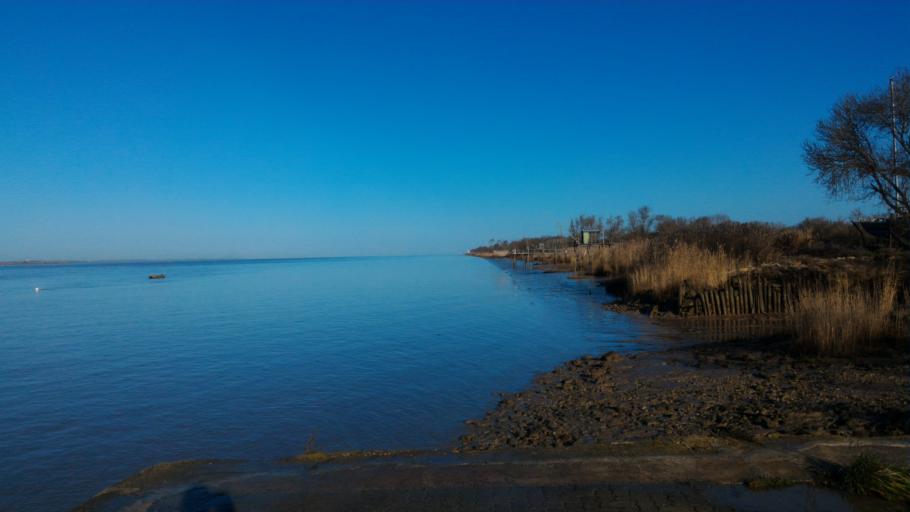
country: FR
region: Aquitaine
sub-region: Departement de la Gironde
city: Saint-Martin-Lacaussade
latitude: 45.1904
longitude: -0.6777
